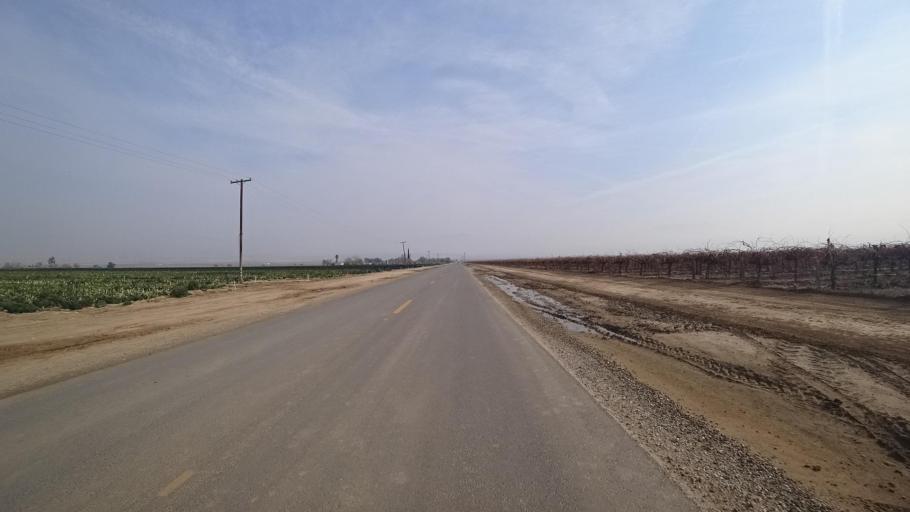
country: US
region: California
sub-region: Kern County
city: Arvin
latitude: 35.0454
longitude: -118.8685
